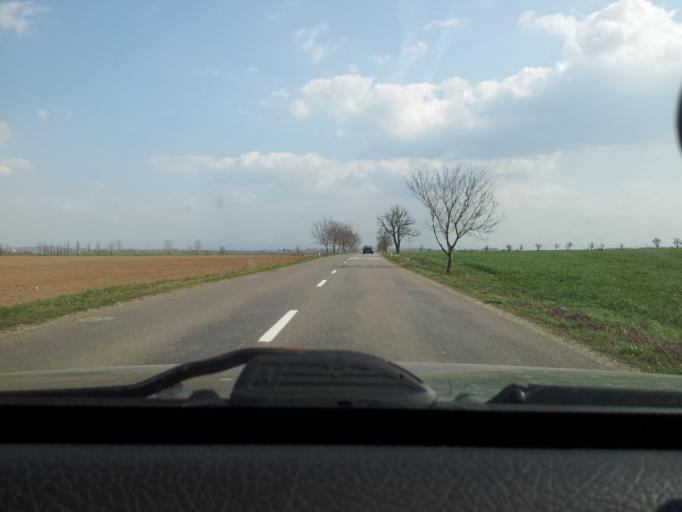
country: SK
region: Nitriansky
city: Tlmace
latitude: 48.2345
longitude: 18.4853
